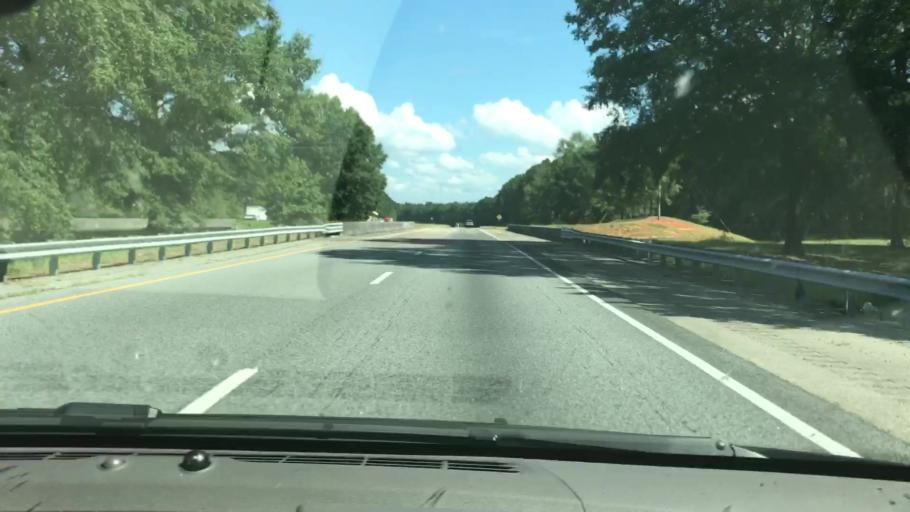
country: US
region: Georgia
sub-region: Harris County
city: Hamilton
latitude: 32.7465
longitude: -85.0177
